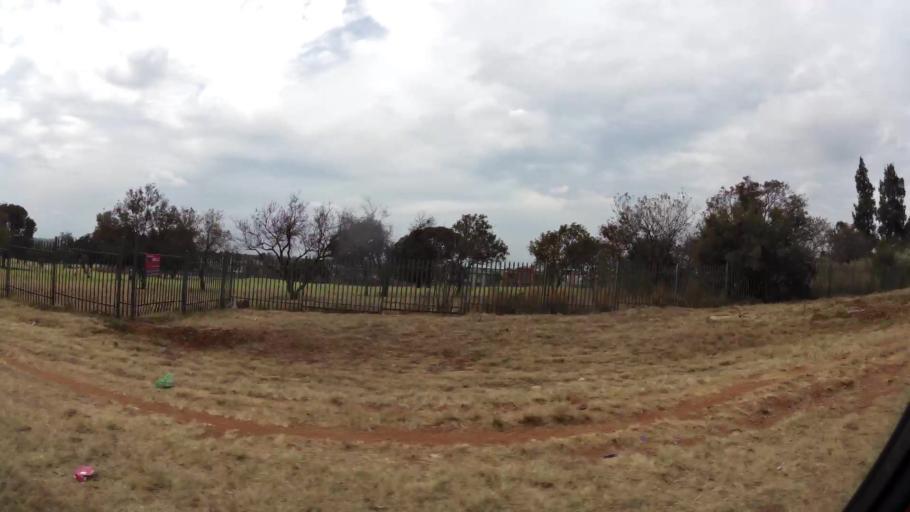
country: ZA
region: Gauteng
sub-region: West Rand District Municipality
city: Muldersdriseloop
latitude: -26.0878
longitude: 27.8682
